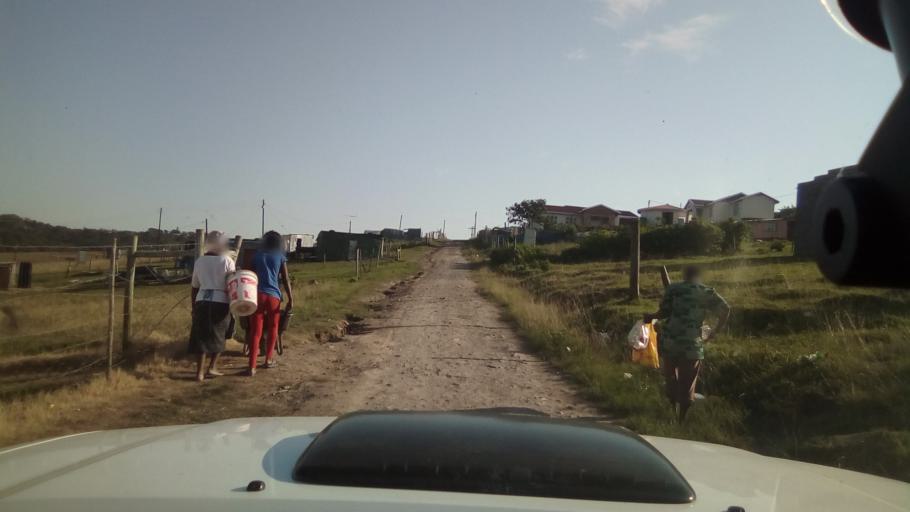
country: ZA
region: Eastern Cape
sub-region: Buffalo City Metropolitan Municipality
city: East London
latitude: -32.8473
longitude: 27.9865
